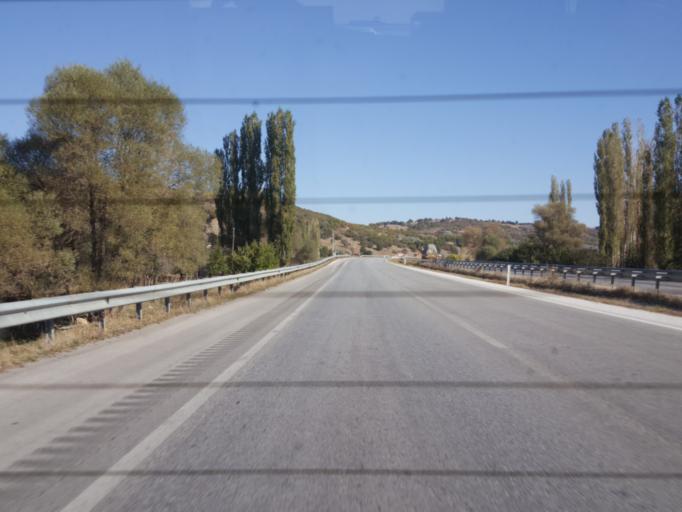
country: TR
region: Corum
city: Alaca
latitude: 40.3037
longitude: 34.6545
